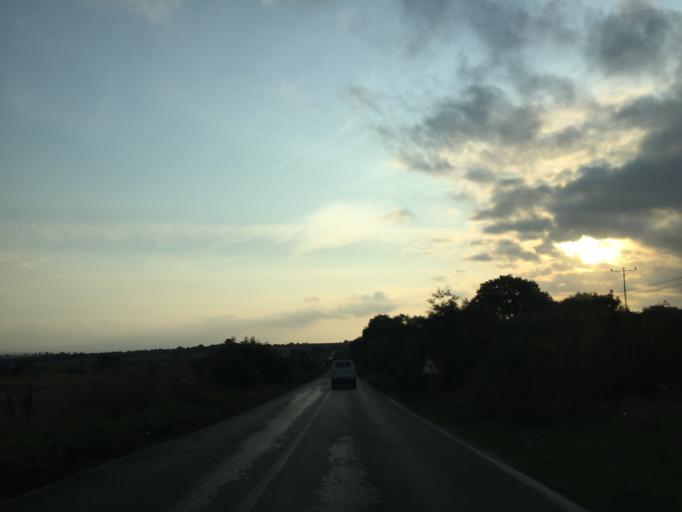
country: TR
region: Balikesir
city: Tutuncu
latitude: 40.1138
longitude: 27.7718
